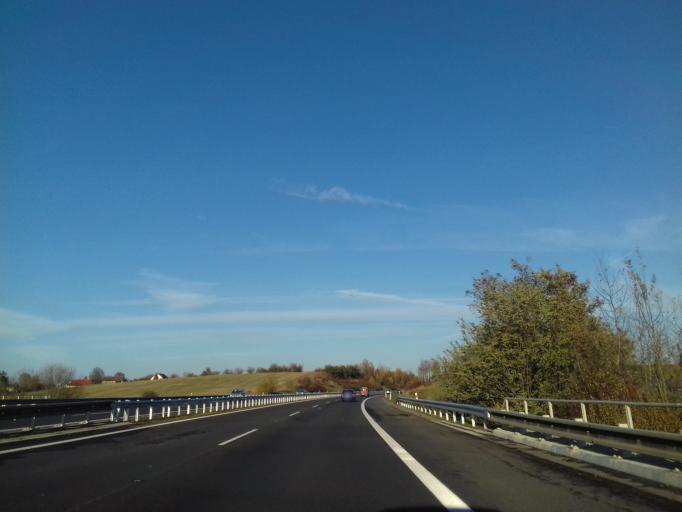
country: CZ
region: Plzensky
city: Myto
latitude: 49.8162
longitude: 13.7622
